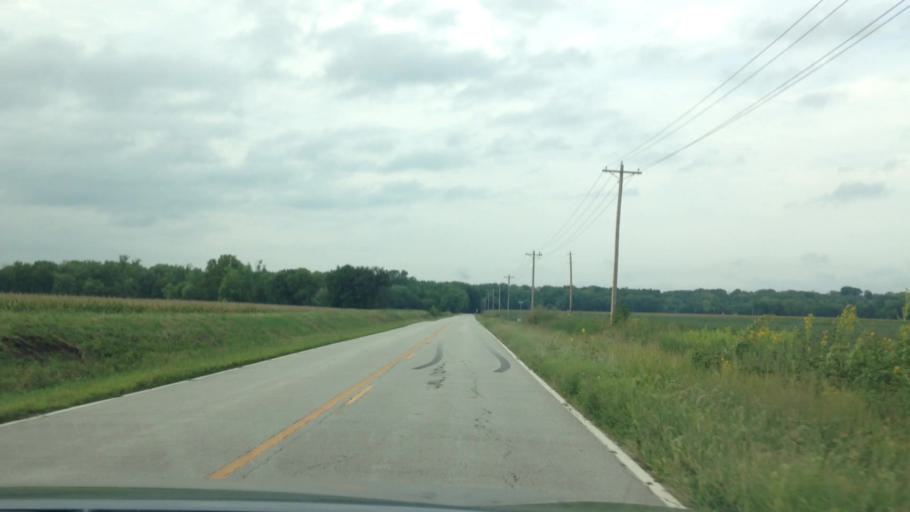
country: US
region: Missouri
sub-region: Clay County
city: Smithville
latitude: 39.3966
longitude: -94.6620
